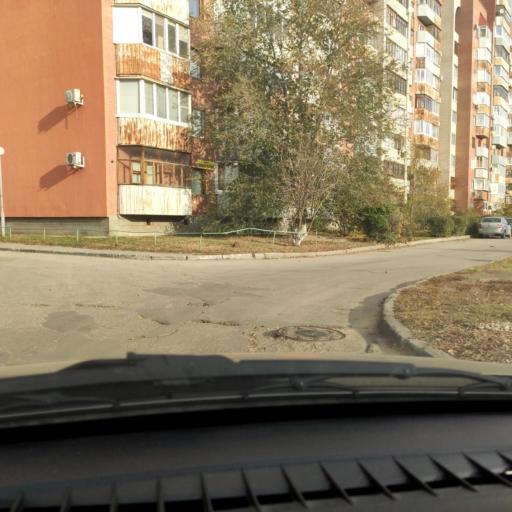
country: RU
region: Samara
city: Tol'yatti
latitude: 53.5444
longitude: 49.3259
